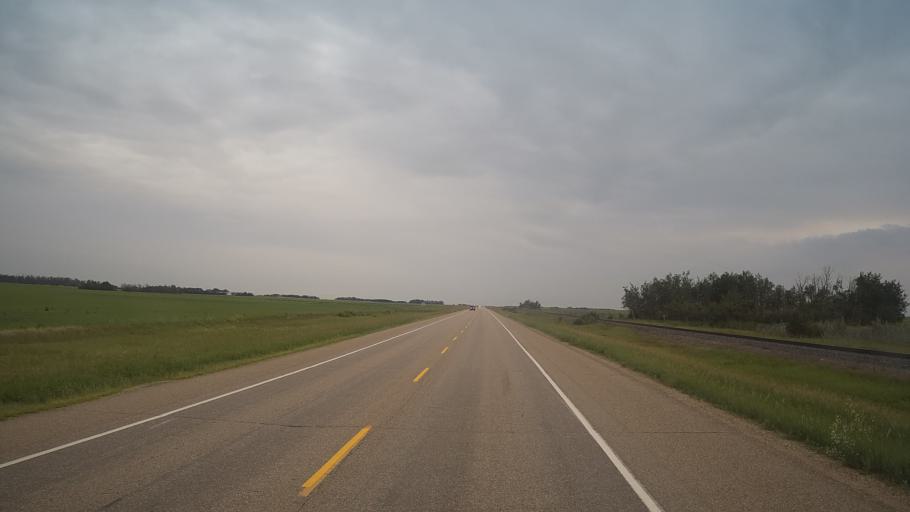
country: CA
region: Saskatchewan
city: Langham
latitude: 52.1254
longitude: -107.2931
